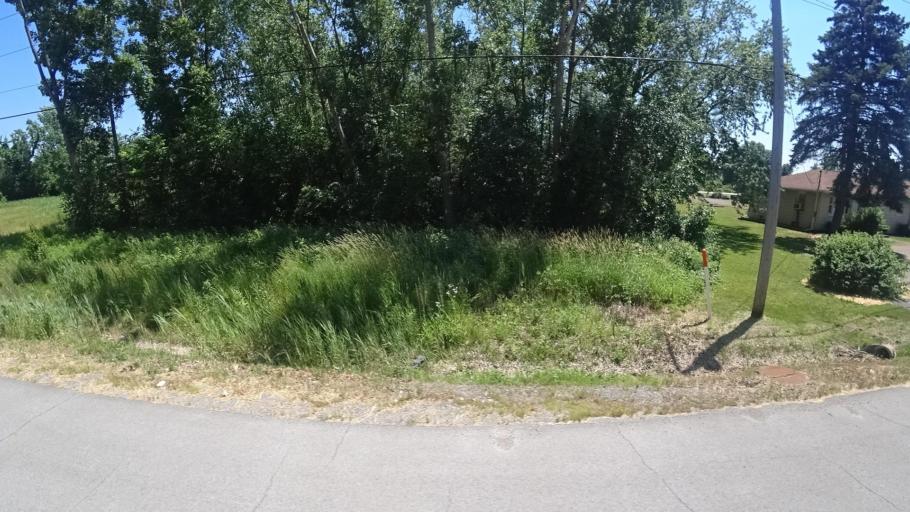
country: US
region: Indiana
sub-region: Porter County
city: Burns Harbor
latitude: 41.6006
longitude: -87.1293
